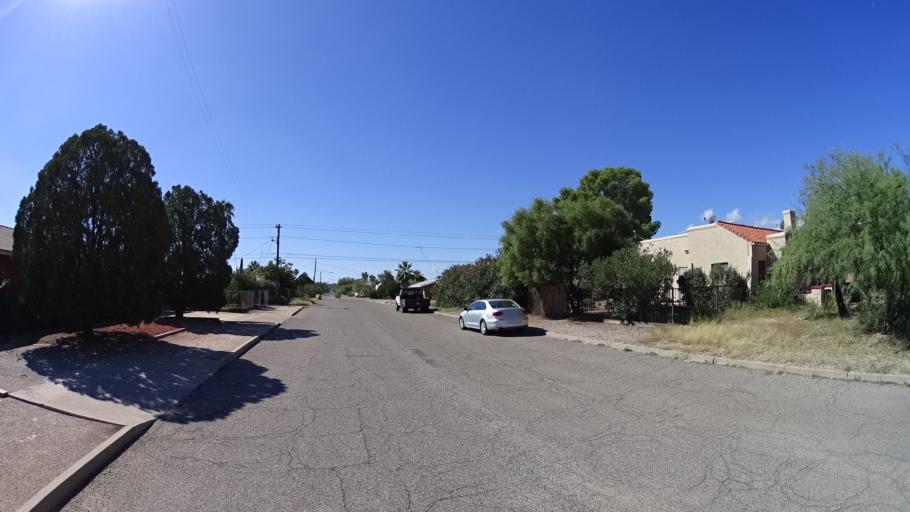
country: US
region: Arizona
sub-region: Pima County
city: Tucson
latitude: 32.2518
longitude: -110.9498
